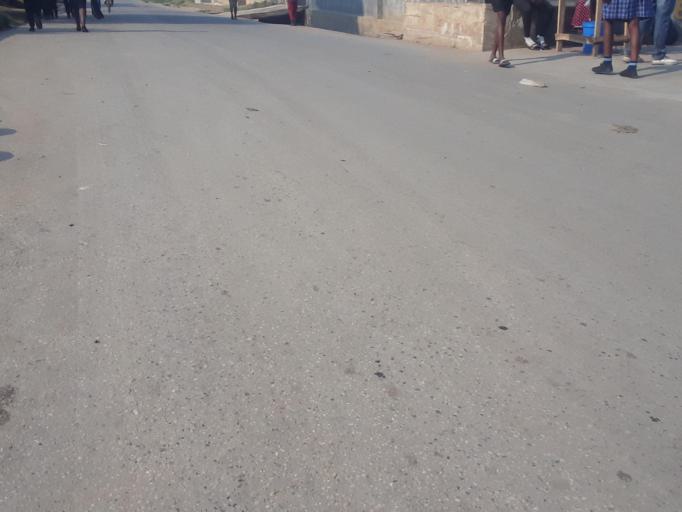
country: ZM
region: Lusaka
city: Lusaka
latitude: -15.3574
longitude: 28.3011
